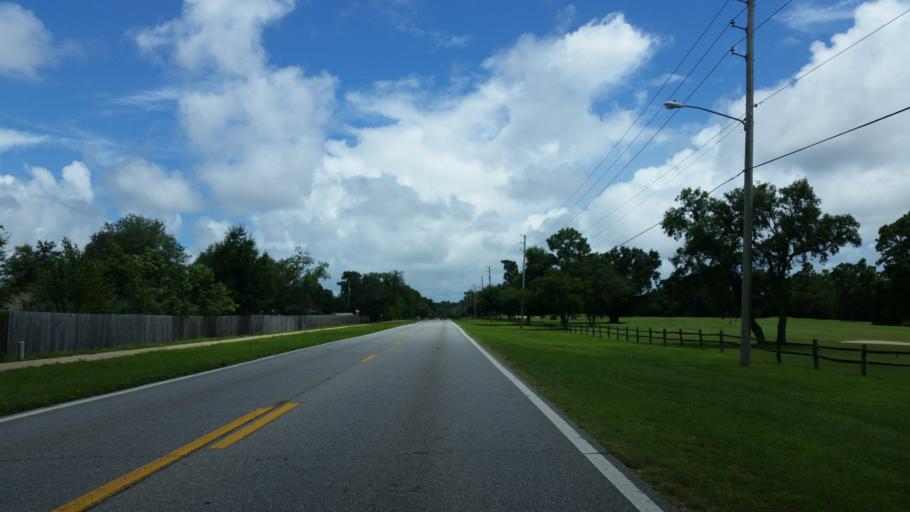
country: US
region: Florida
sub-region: Santa Rosa County
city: Holley
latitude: 30.4428
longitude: -86.9237
